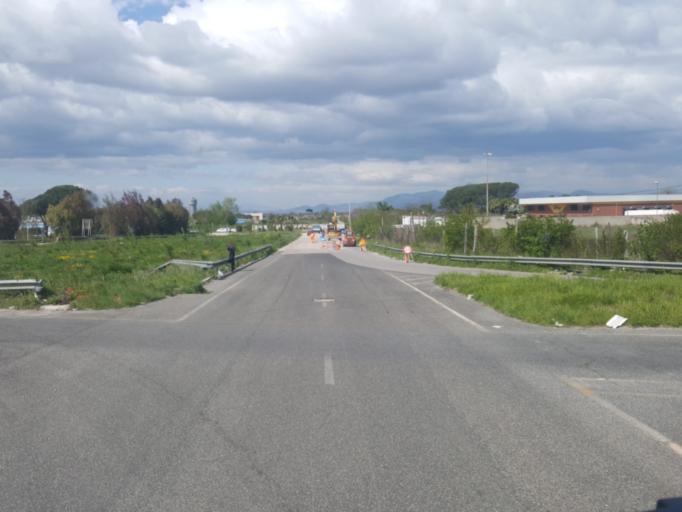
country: IT
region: Campania
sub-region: Provincia di Napoli
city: Torretta-Scalzapecora
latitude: 40.9319
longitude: 14.1225
